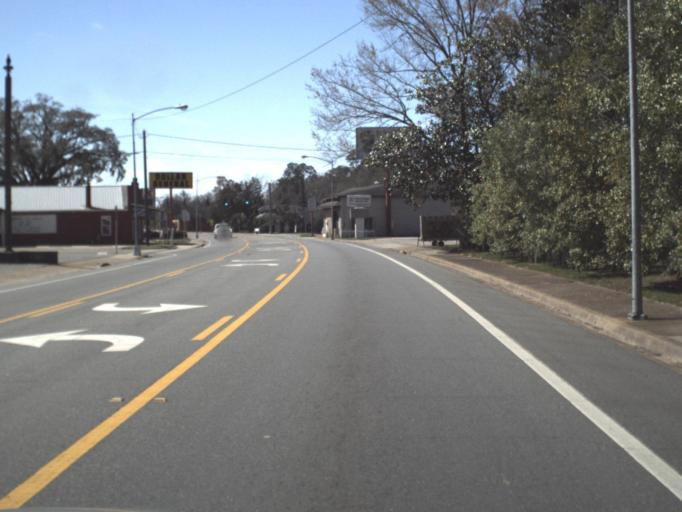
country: US
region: Florida
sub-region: Gadsden County
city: Chattahoochee
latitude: 30.7048
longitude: -84.8414
